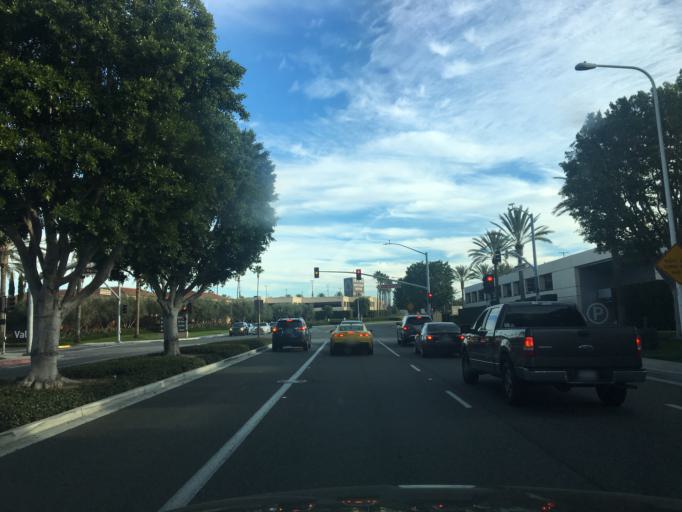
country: US
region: California
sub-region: Orange County
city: Laguna Woods
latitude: 33.6501
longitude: -117.7461
